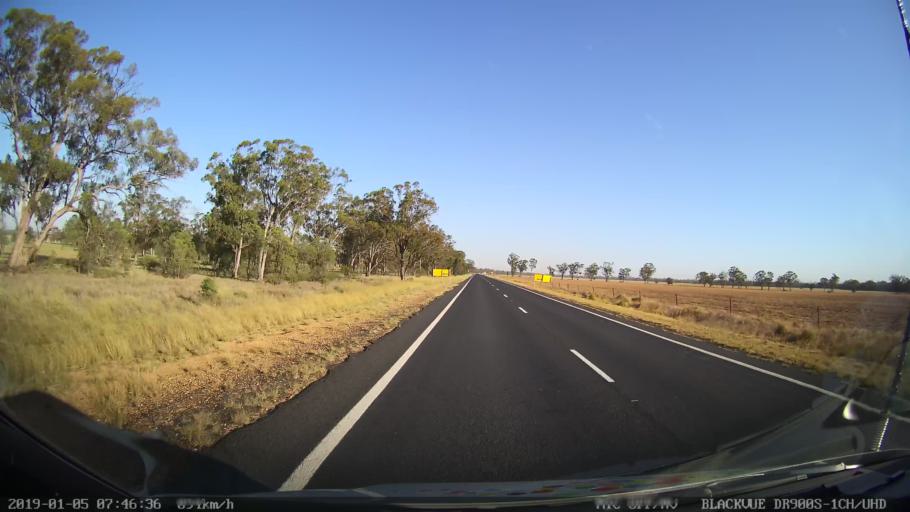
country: AU
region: New South Wales
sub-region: Gilgandra
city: Gilgandra
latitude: -31.8421
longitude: 148.6426
